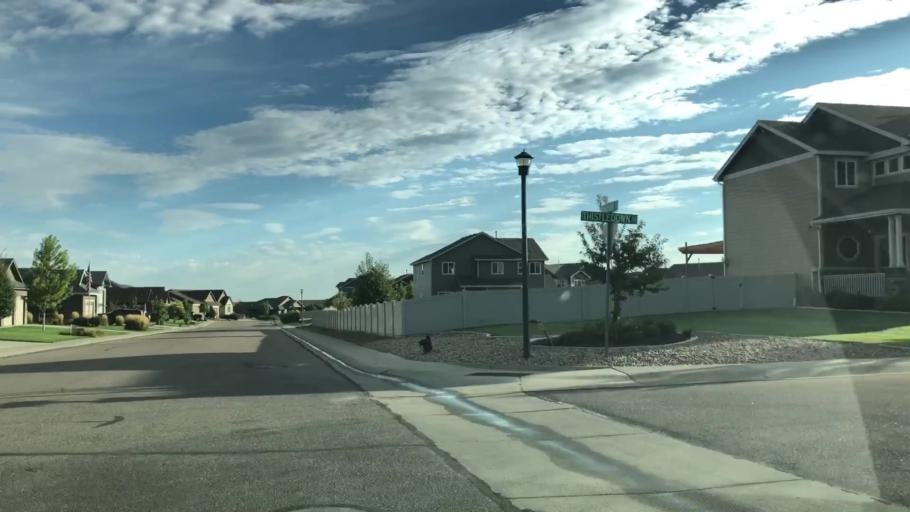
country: US
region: Colorado
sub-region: Weld County
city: Windsor
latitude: 40.4444
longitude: -104.9676
